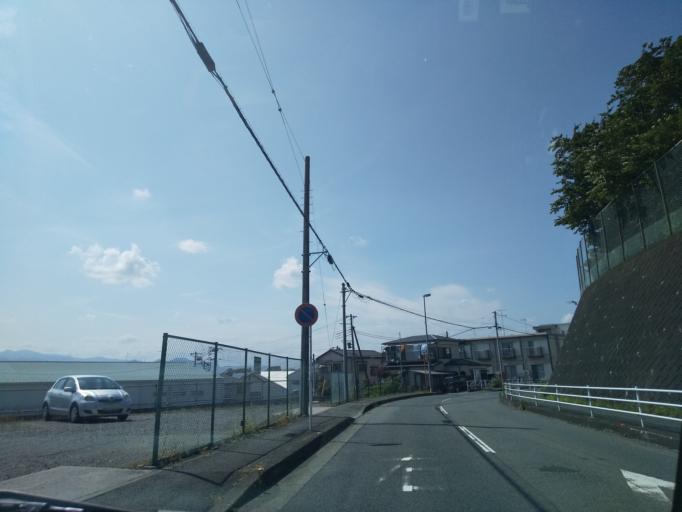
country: JP
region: Kanagawa
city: Minami-rinkan
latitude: 35.4563
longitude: 139.4167
